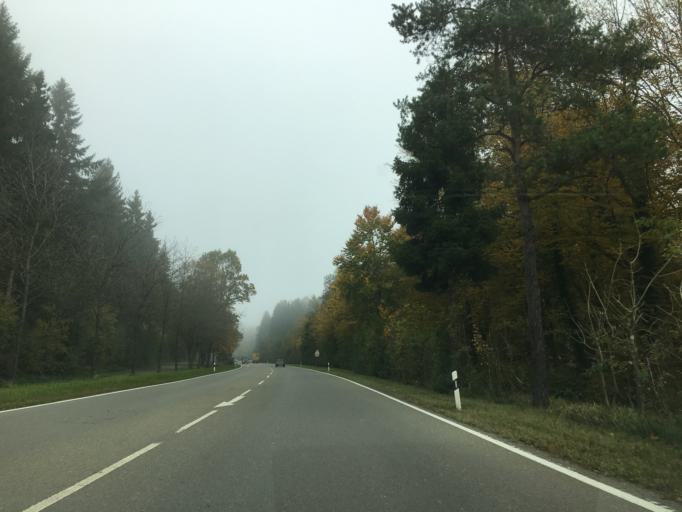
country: DE
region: Baden-Wuerttemberg
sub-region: Freiburg Region
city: Radolfzell am Bodensee
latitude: 47.7567
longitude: 8.9784
